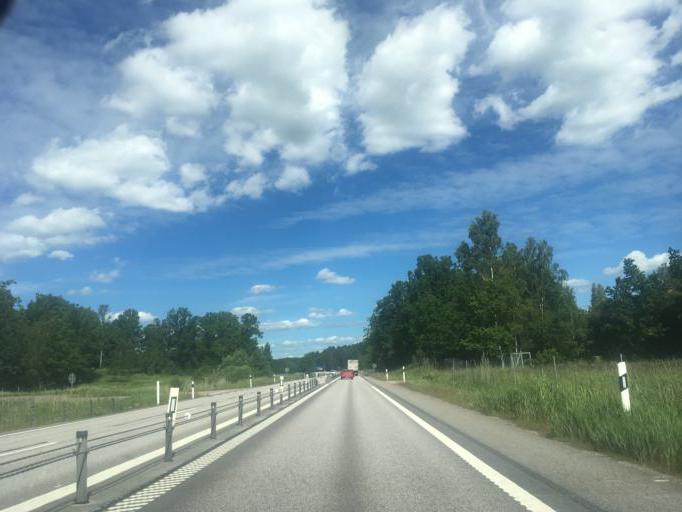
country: SE
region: OEstergoetland
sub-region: Valdemarsviks Kommun
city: Gusum
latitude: 58.3744
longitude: 16.4251
